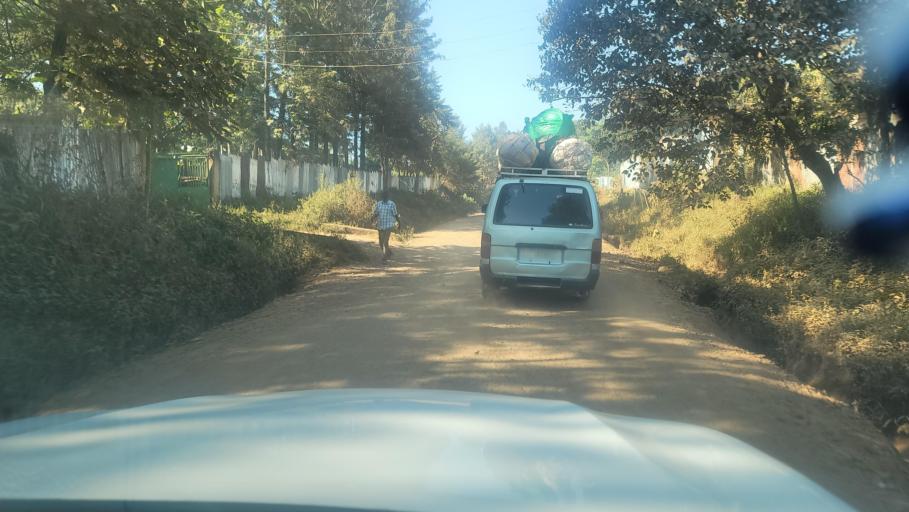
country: ET
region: Oromiya
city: Agaro
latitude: 7.8600
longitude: 36.5757
